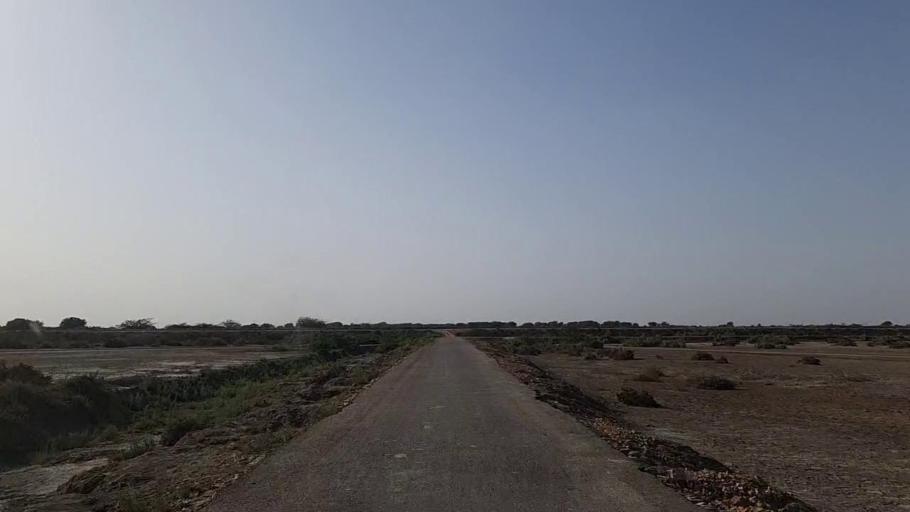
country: PK
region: Sindh
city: Jati
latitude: 24.3037
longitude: 68.1962
